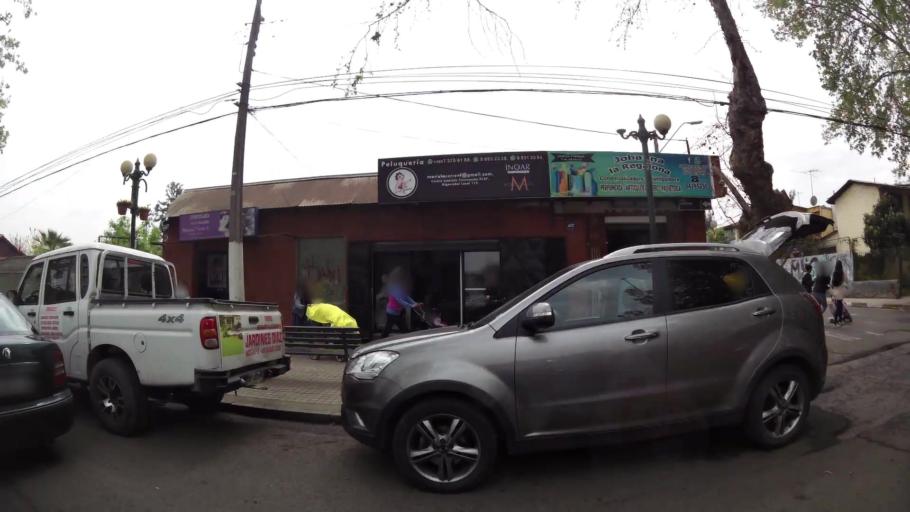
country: CL
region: Santiago Metropolitan
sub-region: Provincia de Chacabuco
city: Chicureo Abajo
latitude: -33.2046
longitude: -70.6742
